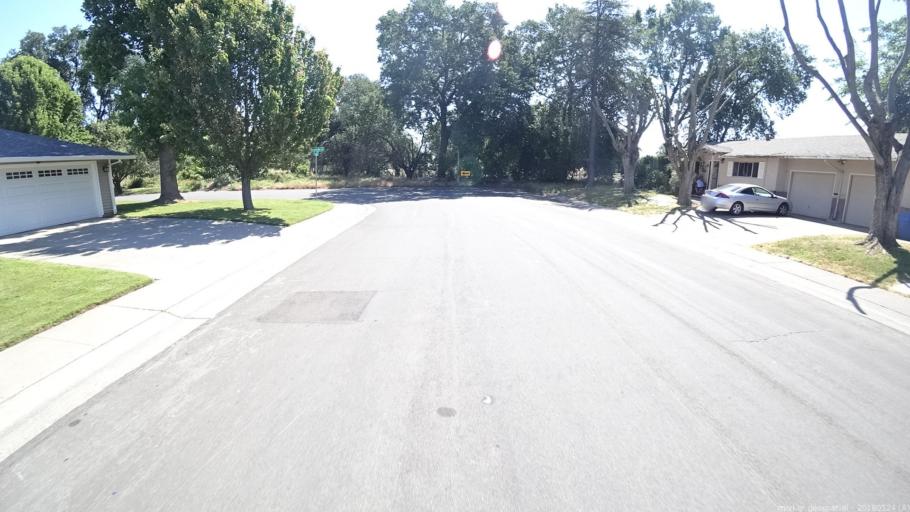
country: US
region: California
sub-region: Sacramento County
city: Sacramento
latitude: 38.6007
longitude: -121.4604
